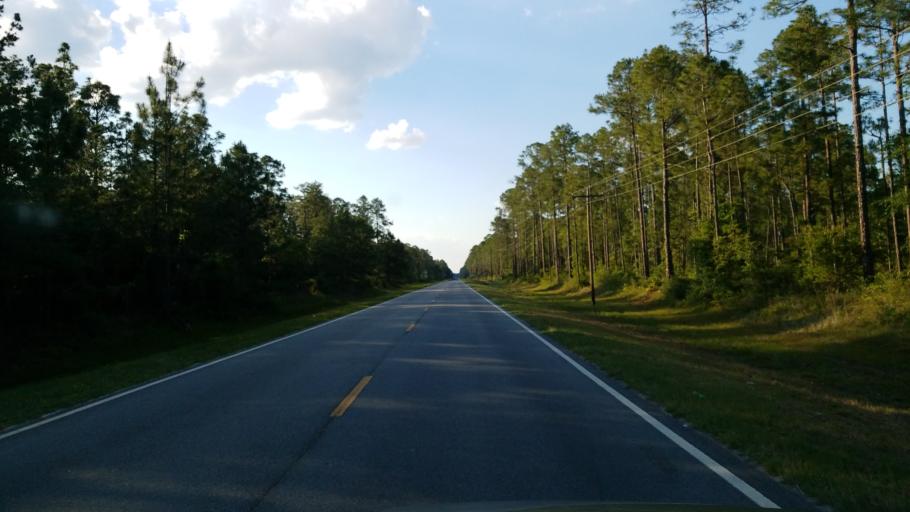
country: US
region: Georgia
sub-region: Lanier County
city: Lakeland
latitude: 31.1005
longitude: -83.0794
